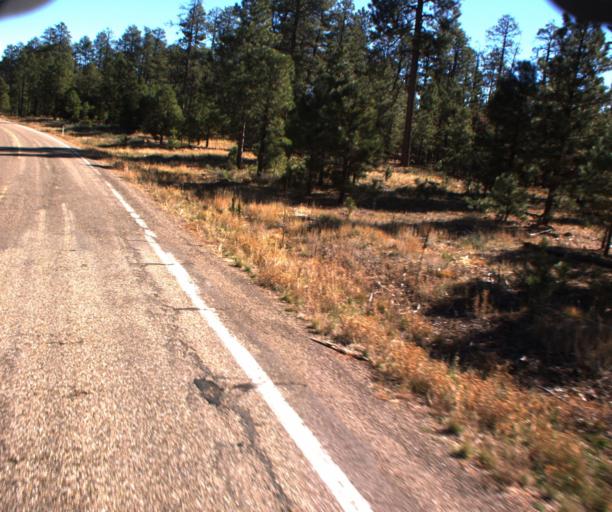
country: US
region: Arizona
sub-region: Coconino County
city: Fredonia
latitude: 36.7350
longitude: -112.2224
